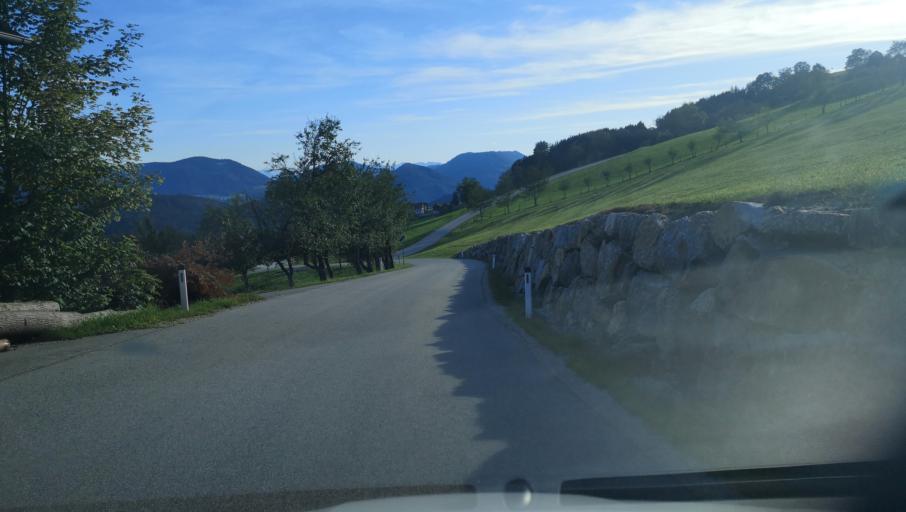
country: AT
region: Lower Austria
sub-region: Politischer Bezirk Amstetten
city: Allhartsberg
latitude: 47.9814
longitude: 14.8375
